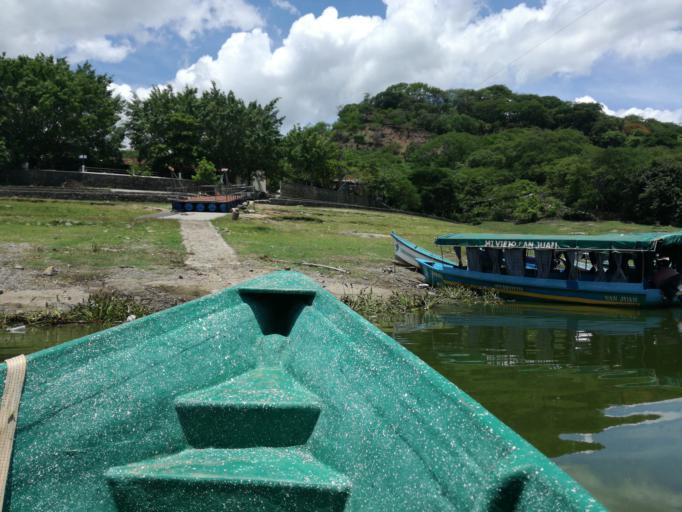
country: SV
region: Cuscatlan
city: Suchitoto
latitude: 13.9471
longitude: -89.0170
